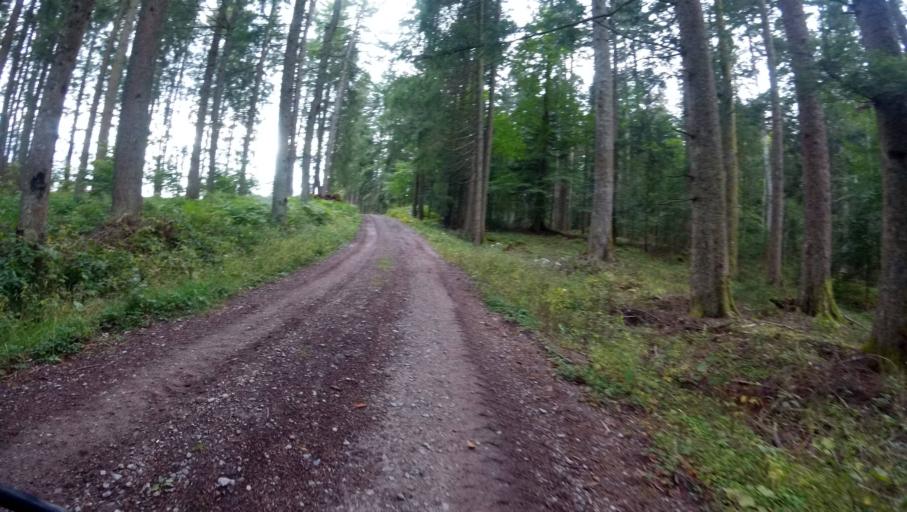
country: DE
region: Baden-Wuerttemberg
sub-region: Karlsruhe Region
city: Enzklosterle
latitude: 48.6044
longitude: 8.4359
